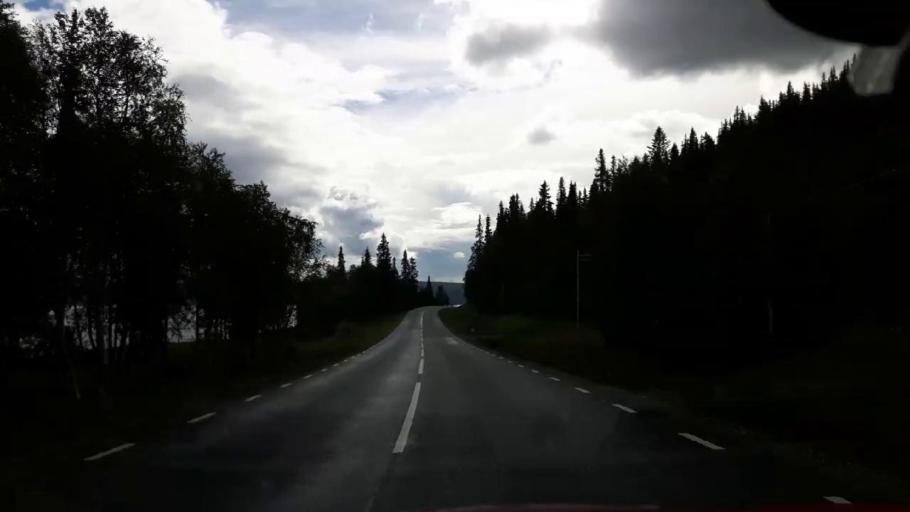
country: NO
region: Nord-Trondelag
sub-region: Royrvik
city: Royrvik
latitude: 64.8329
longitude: 14.0773
